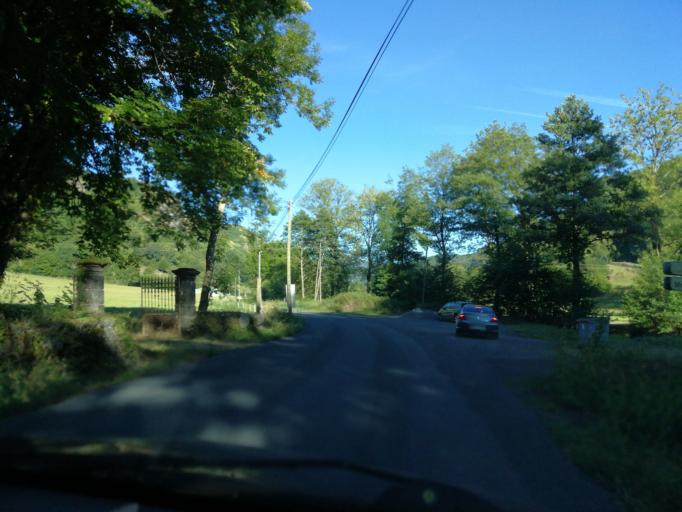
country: FR
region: Auvergne
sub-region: Departement du Cantal
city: Saint-Cernin
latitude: 45.1087
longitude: 2.5110
